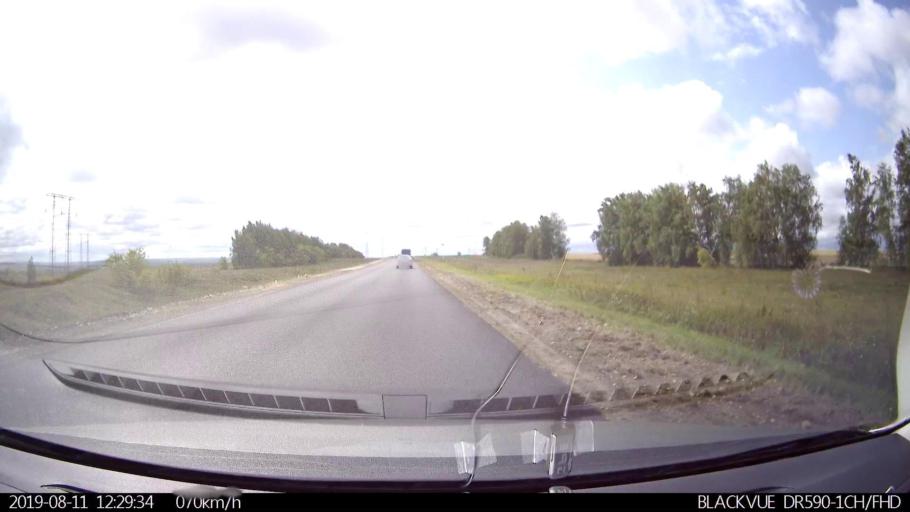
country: RU
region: Ulyanovsk
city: Ignatovka
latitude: 53.8333
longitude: 47.9016
